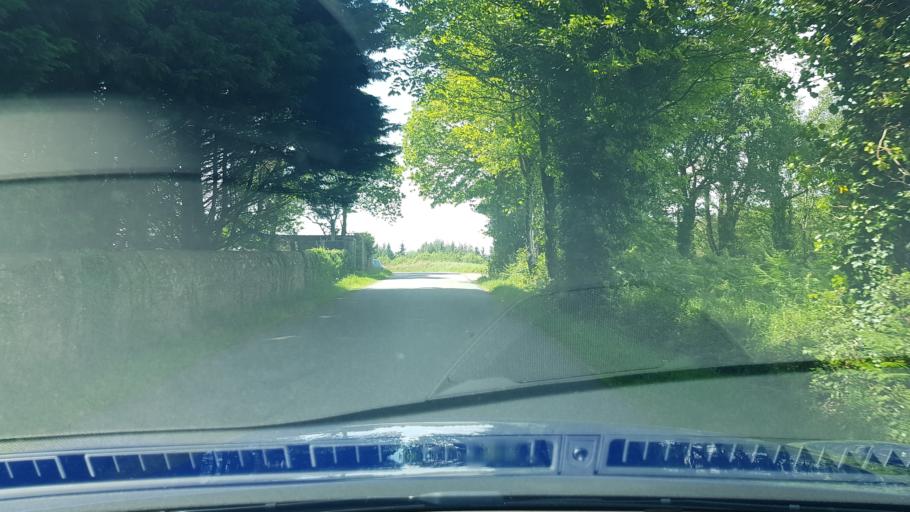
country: FR
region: Brittany
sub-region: Departement du Morbihan
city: Guidel-Plage
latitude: 47.8050
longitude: -3.5027
